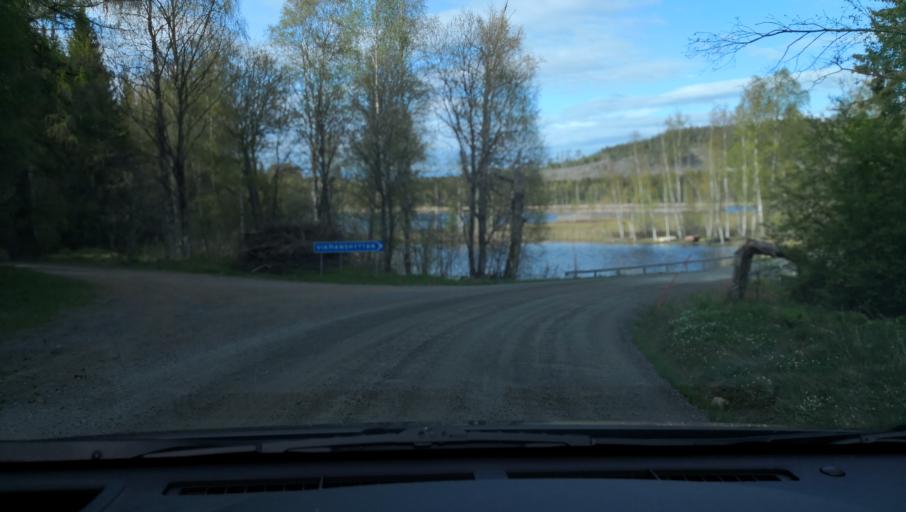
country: SE
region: Dalarna
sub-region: Saters Kommun
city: Saeter
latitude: 60.2712
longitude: 15.8276
